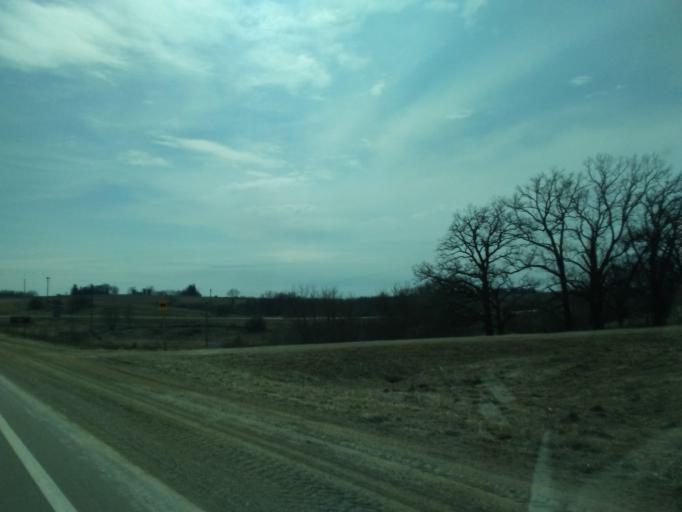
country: US
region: Minnesota
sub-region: Fillmore County
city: Harmony
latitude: 43.4596
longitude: -91.8695
